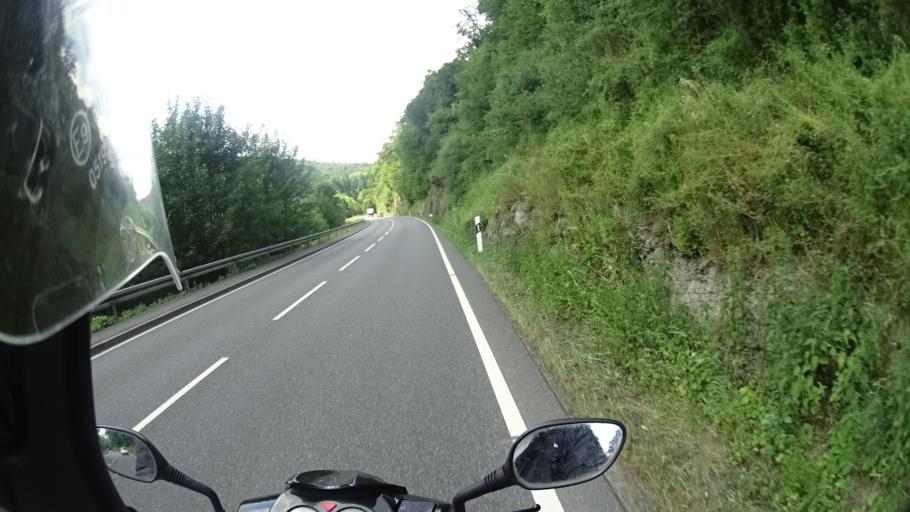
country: DE
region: Hesse
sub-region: Regierungsbezirk Darmstadt
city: Bad Schwalbach
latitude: 50.1541
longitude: 8.0800
